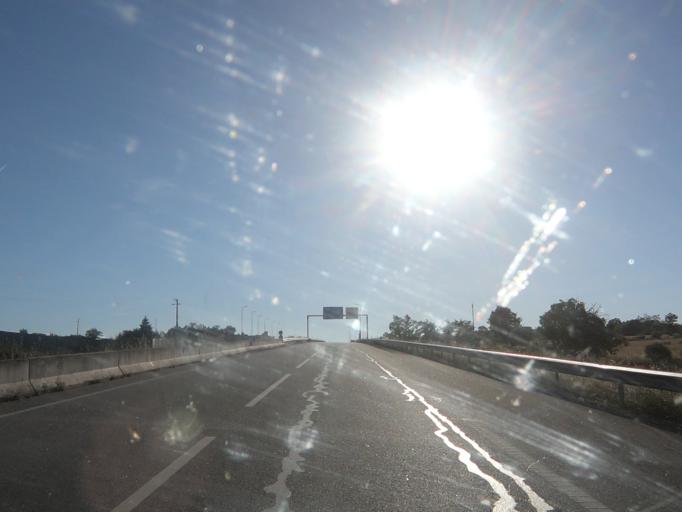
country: PT
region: Guarda
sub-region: Pinhel
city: Pinhel
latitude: 40.6045
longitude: -7.0608
